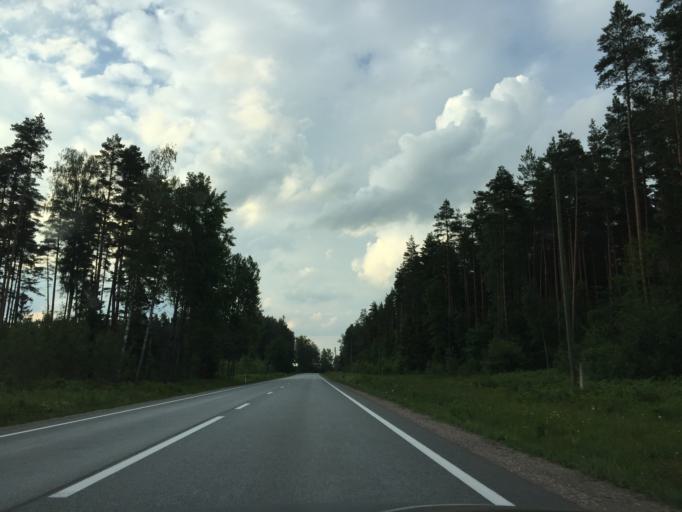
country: LV
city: Tireli
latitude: 56.8665
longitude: 23.6212
